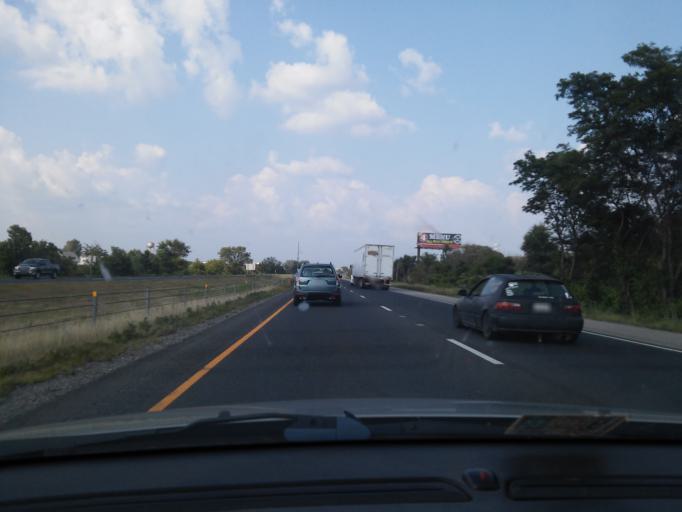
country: US
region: Illinois
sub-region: Will County
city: Rockdale
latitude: 41.5011
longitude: -88.1562
